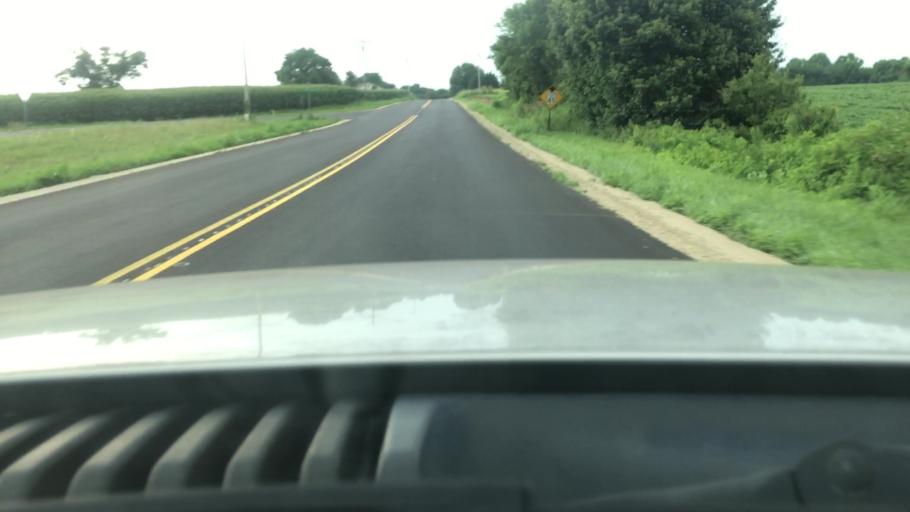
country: US
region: North Carolina
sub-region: Surry County
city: Dobson
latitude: 36.3955
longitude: -80.7918
